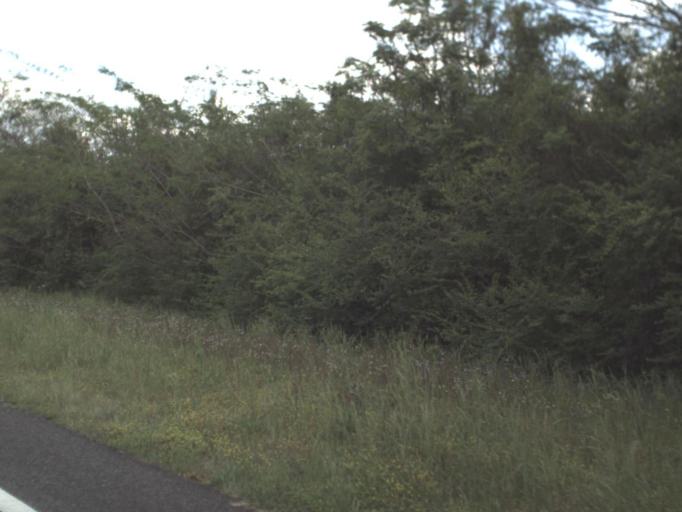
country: US
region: Florida
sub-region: Escambia County
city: Molino
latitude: 30.7545
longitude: -87.3451
